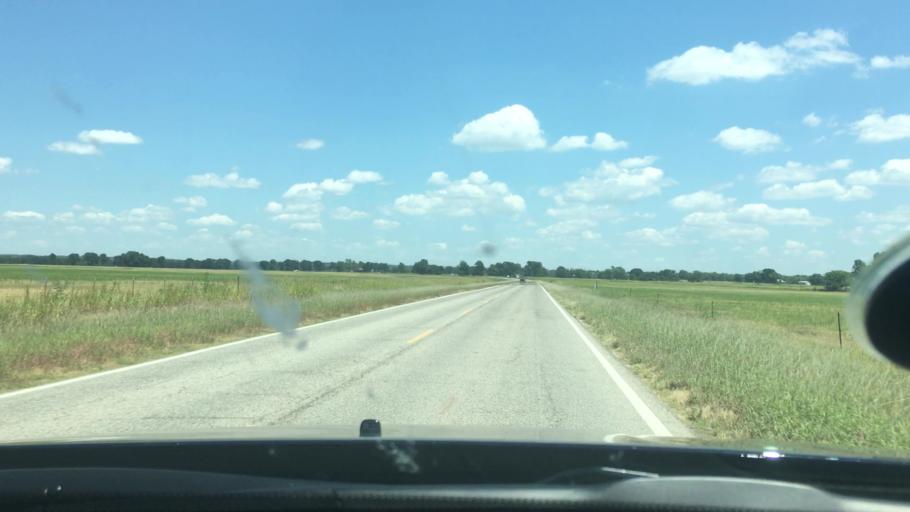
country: US
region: Oklahoma
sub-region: Carter County
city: Dickson
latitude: 34.2460
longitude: -96.9722
